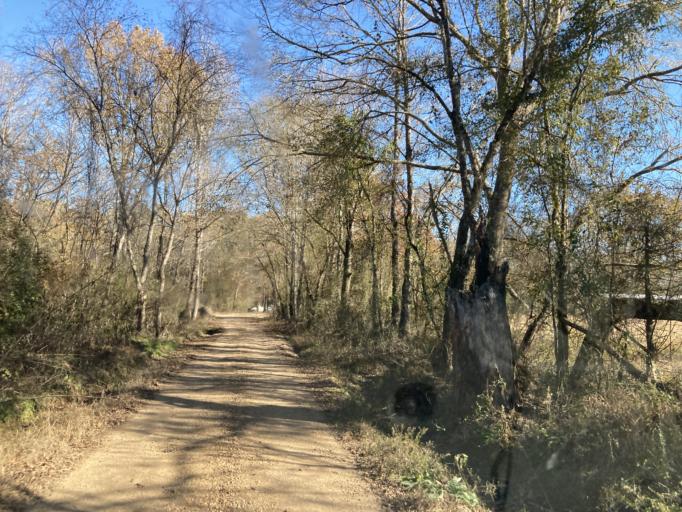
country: US
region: Mississippi
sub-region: Holmes County
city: Pickens
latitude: 32.8578
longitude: -90.0043
